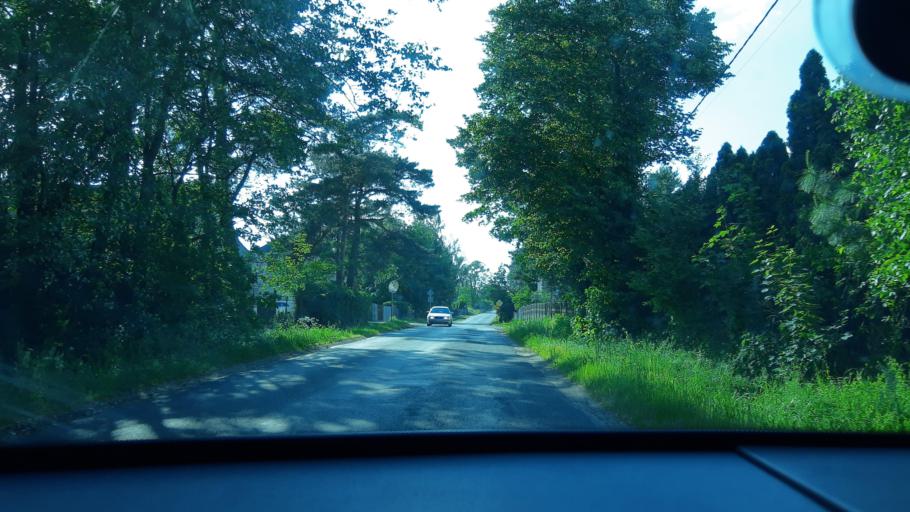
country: PL
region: Lodz Voivodeship
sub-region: Powiat sieradzki
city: Sieradz
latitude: 51.5457
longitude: 18.7828
